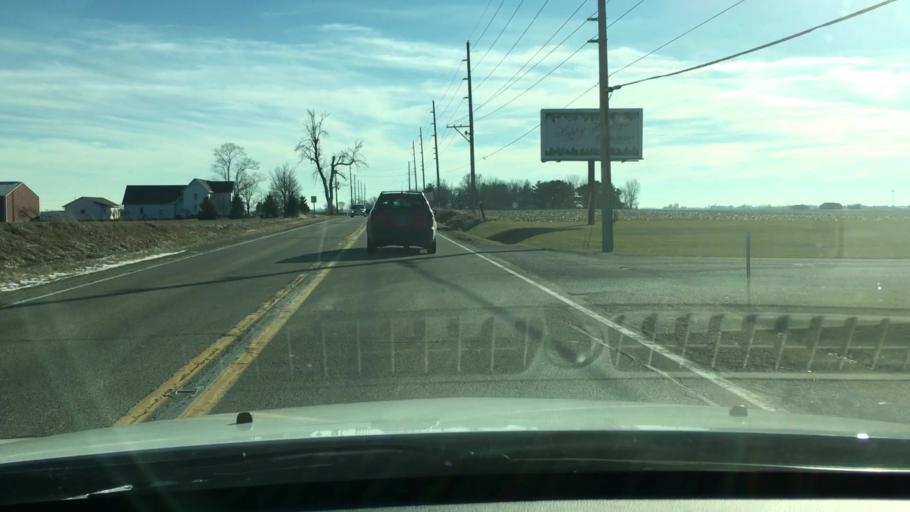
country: US
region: Illinois
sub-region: LaSalle County
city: Mendota
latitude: 41.5360
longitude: -89.1277
